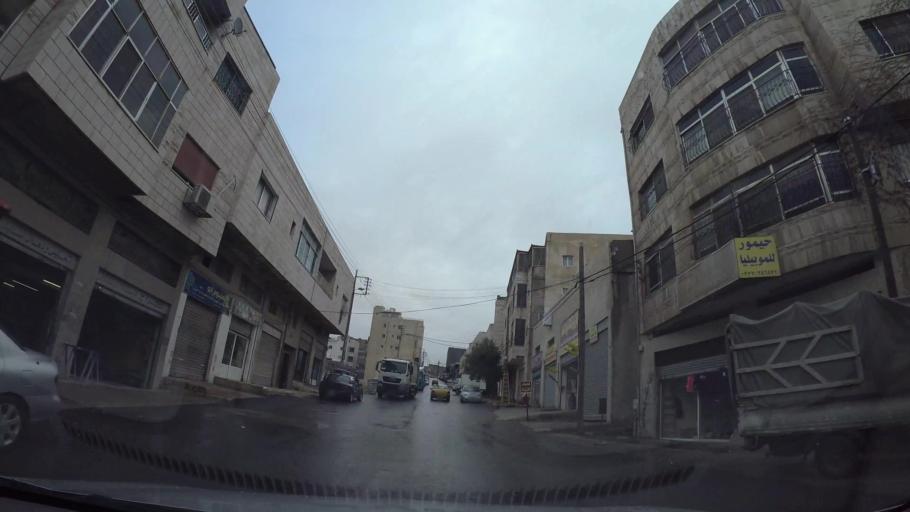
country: JO
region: Amman
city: Al Jubayhah
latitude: 32.0291
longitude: 35.8385
